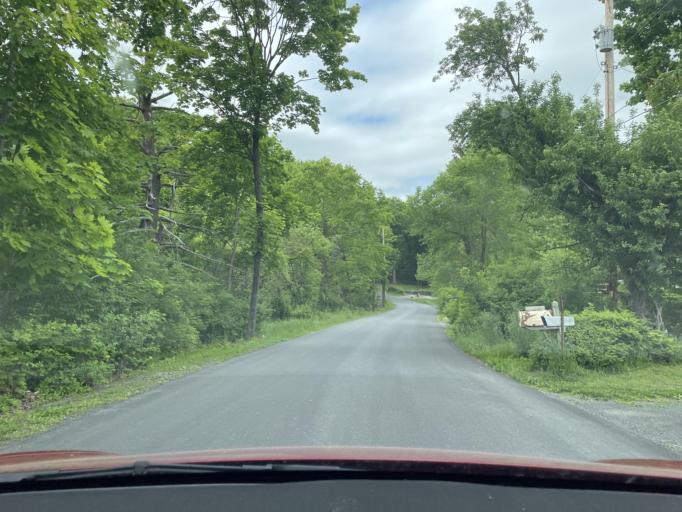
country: US
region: New York
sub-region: Ulster County
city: Woodstock
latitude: 42.0235
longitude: -74.1075
